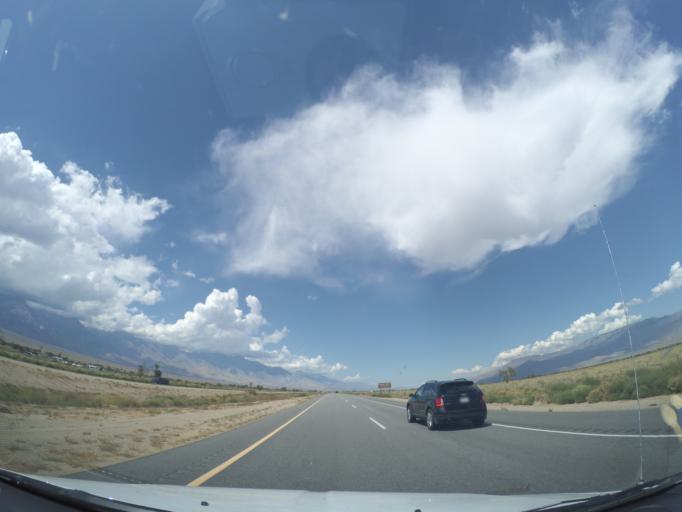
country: US
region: California
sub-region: Inyo County
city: Lone Pine
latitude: 36.7281
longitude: -118.1442
